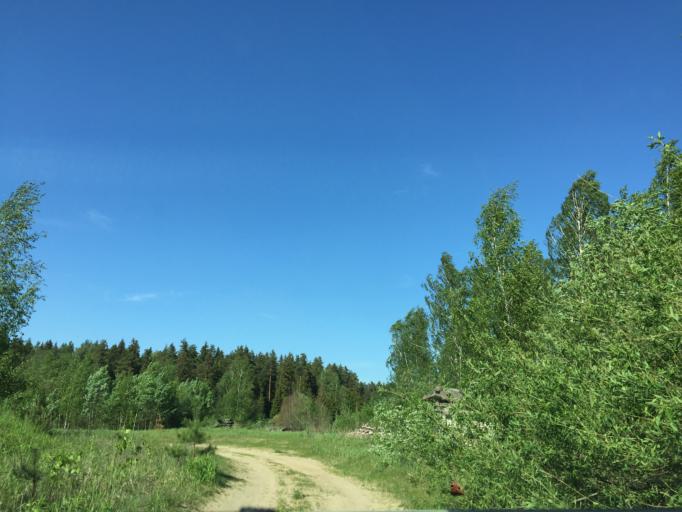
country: LV
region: Ozolnieku
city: Ozolnieki
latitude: 56.6691
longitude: 23.8094
